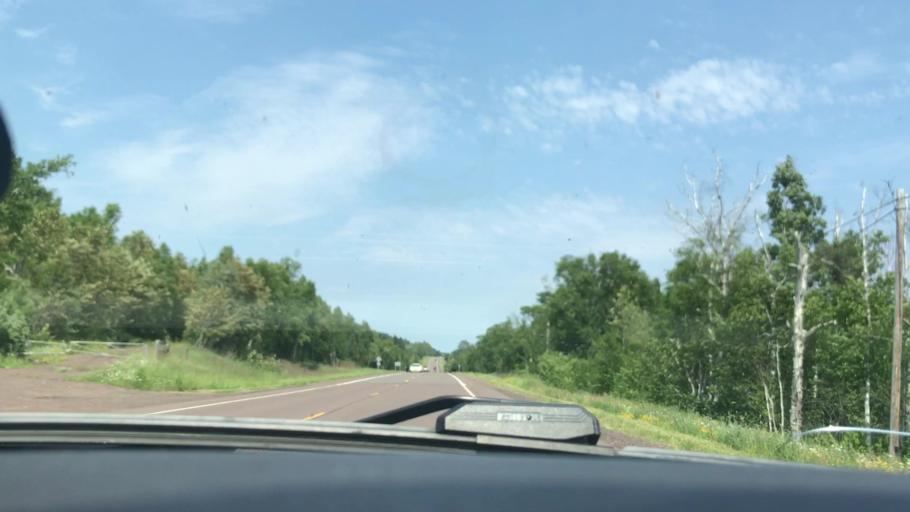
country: US
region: Minnesota
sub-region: Lake County
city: Silver Bay
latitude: 47.4401
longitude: -91.0742
